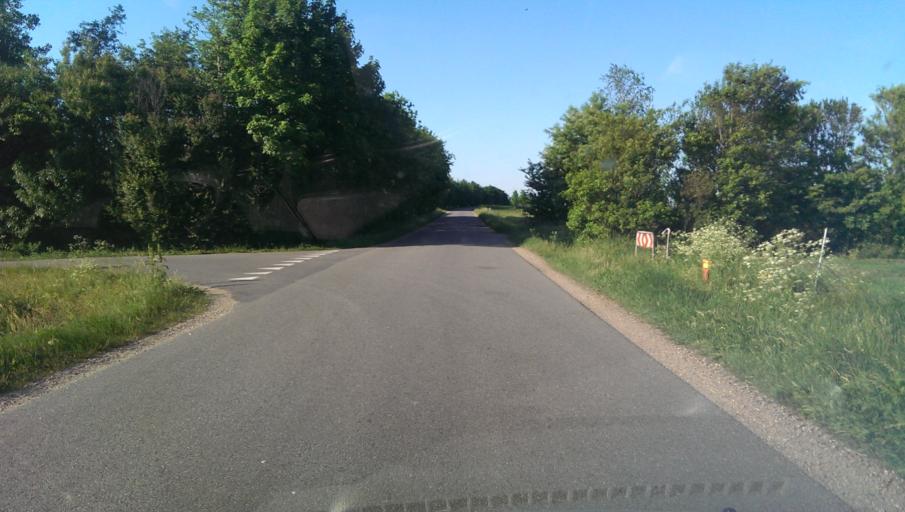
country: DK
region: South Denmark
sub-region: Esbjerg Kommune
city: Bramming
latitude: 55.5482
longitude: 8.7057
